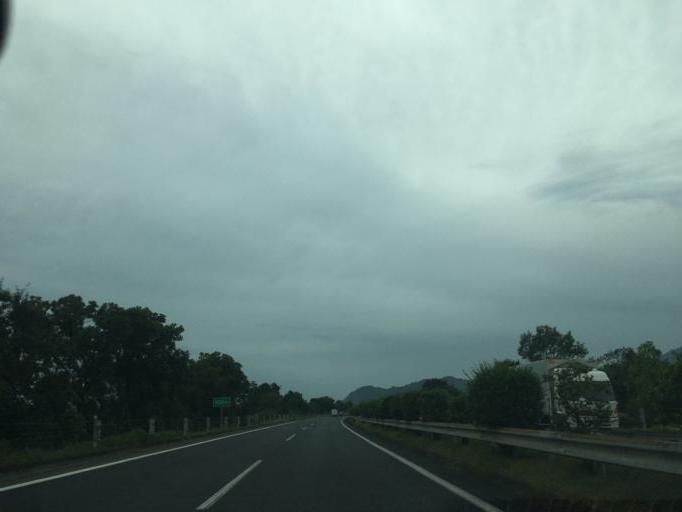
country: JP
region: Saga Prefecture
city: Saga-shi
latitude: 33.3075
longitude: 130.2398
